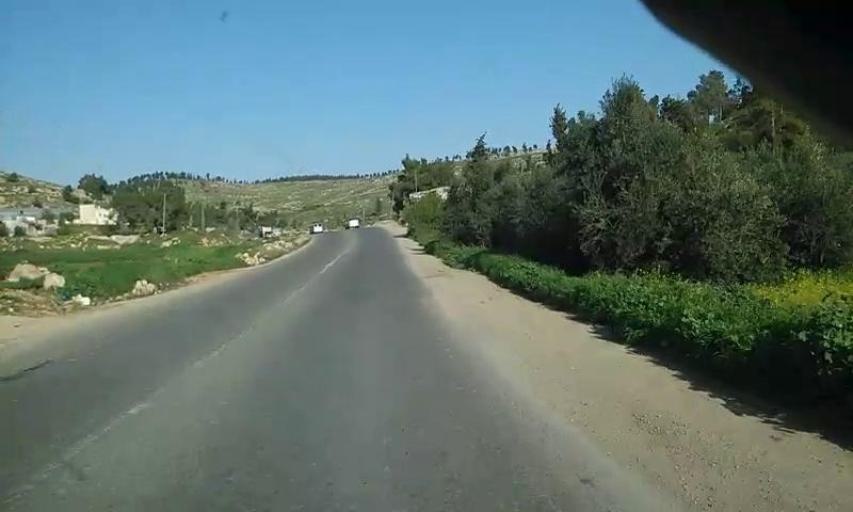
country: PS
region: West Bank
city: Ar Rihiyah
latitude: 31.4871
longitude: 35.0611
